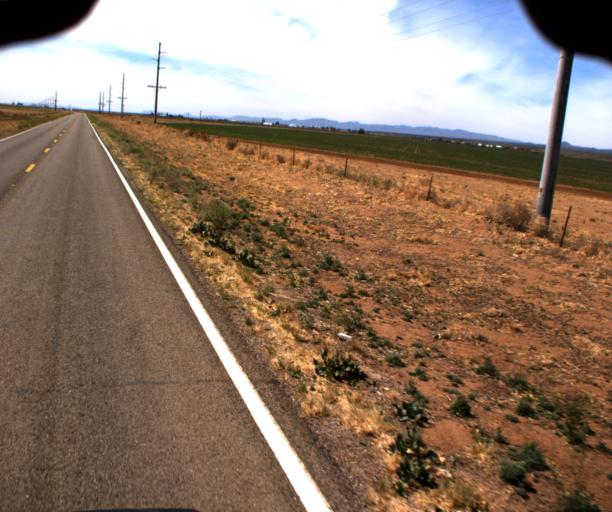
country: US
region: Arizona
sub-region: Cochise County
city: Tombstone
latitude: 31.8235
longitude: -109.6952
